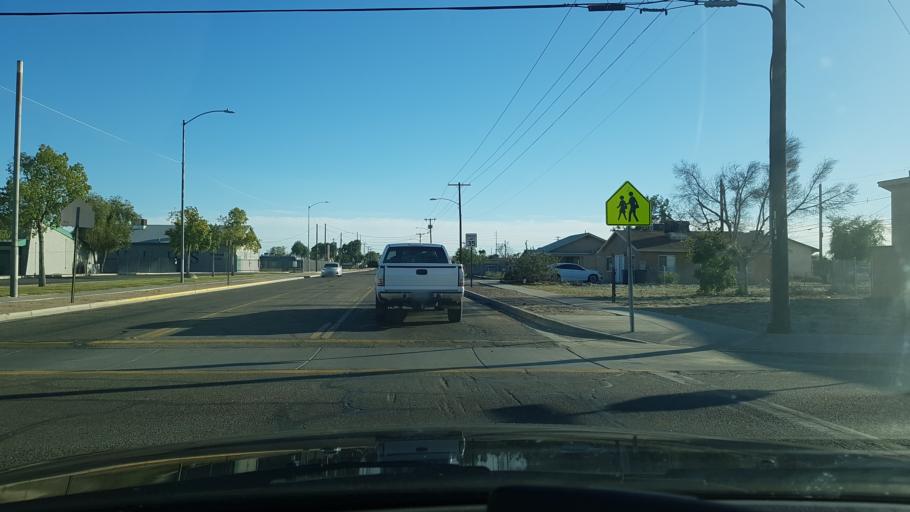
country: US
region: Arizona
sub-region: Yuma County
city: Yuma
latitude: 32.6877
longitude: -114.6160
